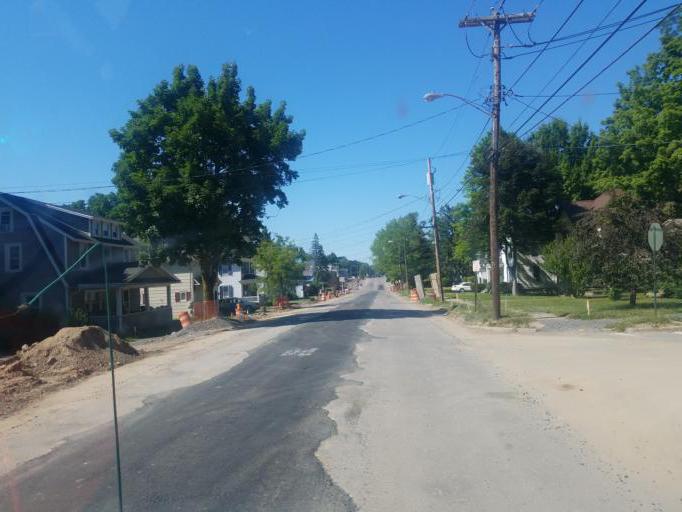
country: US
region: New York
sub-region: Wayne County
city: Newark
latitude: 43.0378
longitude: -77.0962
